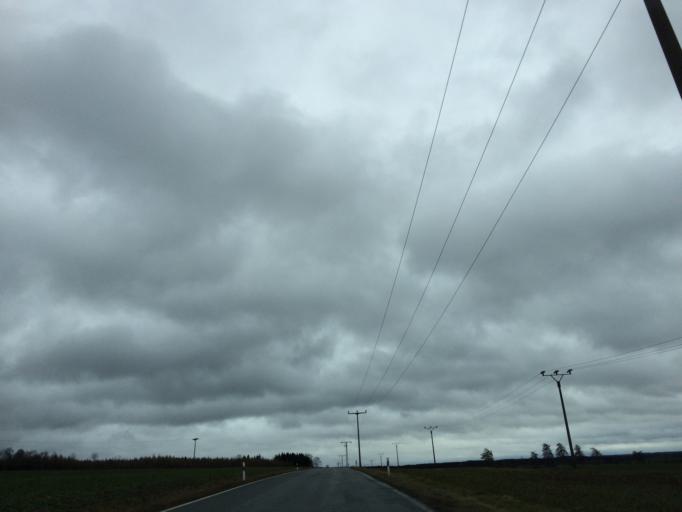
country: DE
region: Thuringia
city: Dreba
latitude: 50.6785
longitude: 11.7388
